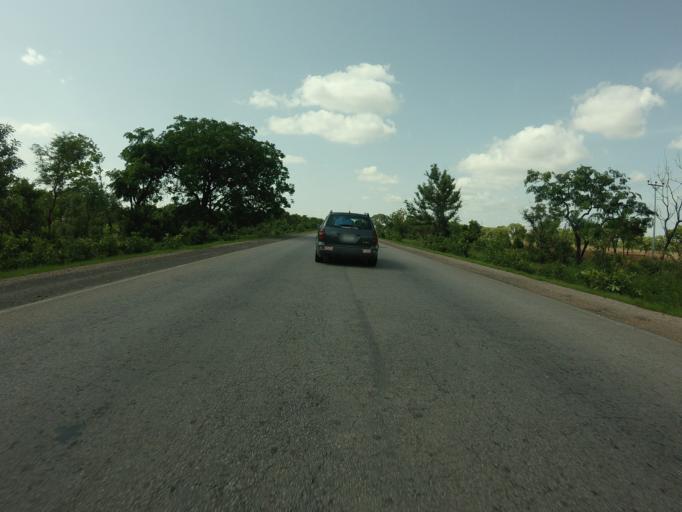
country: GH
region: Northern
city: Savelugu
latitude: 9.9441
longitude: -0.8394
